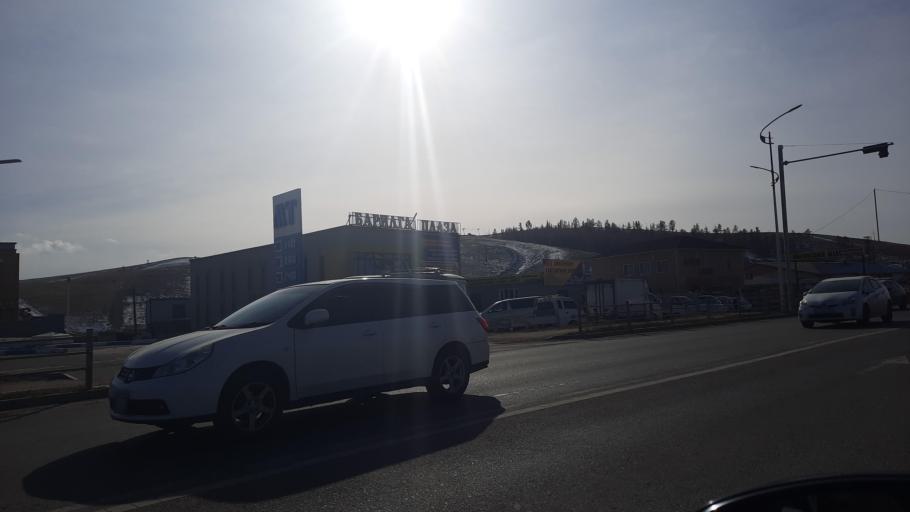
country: MN
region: Orhon
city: Erdenet
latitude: 49.0247
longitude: 104.0620
